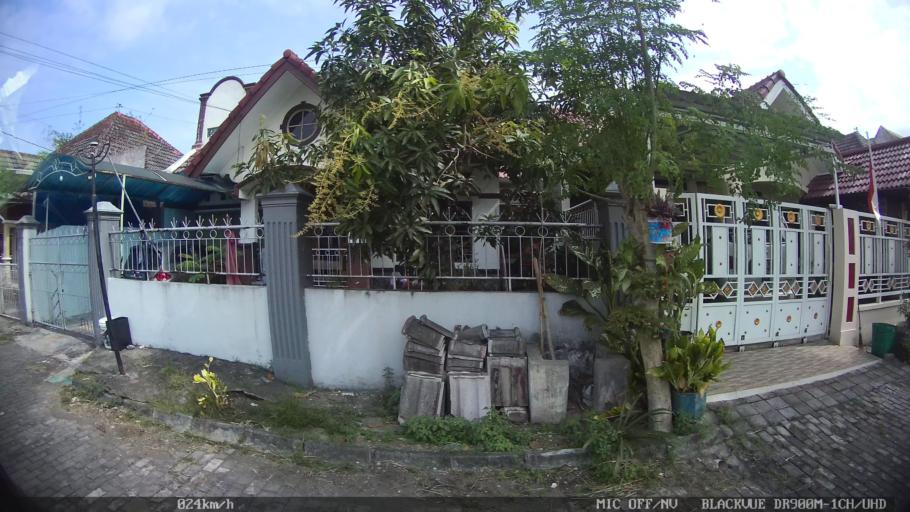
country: ID
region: Daerah Istimewa Yogyakarta
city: Depok
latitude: -7.7587
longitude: 110.4206
